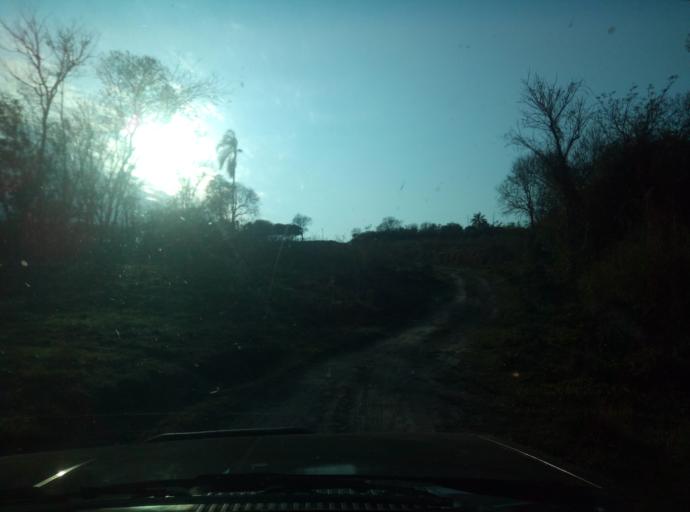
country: PY
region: Caaguazu
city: Doctor Cecilio Baez
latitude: -25.1989
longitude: -56.1197
